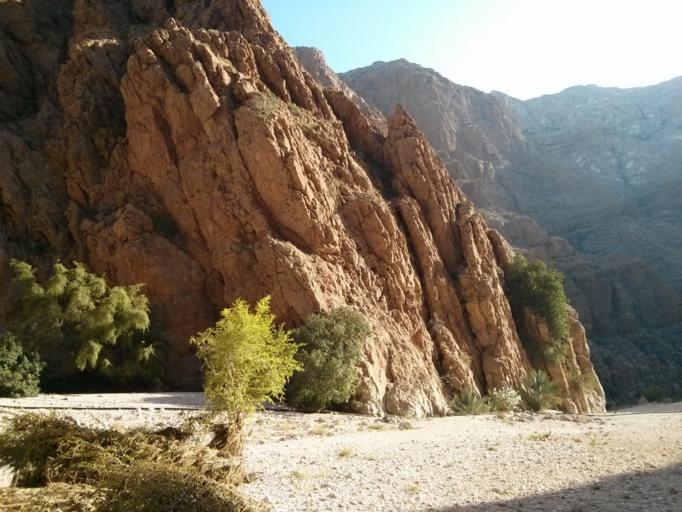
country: OM
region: Ash Sharqiyah
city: Sur
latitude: 22.8359
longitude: 59.2392
